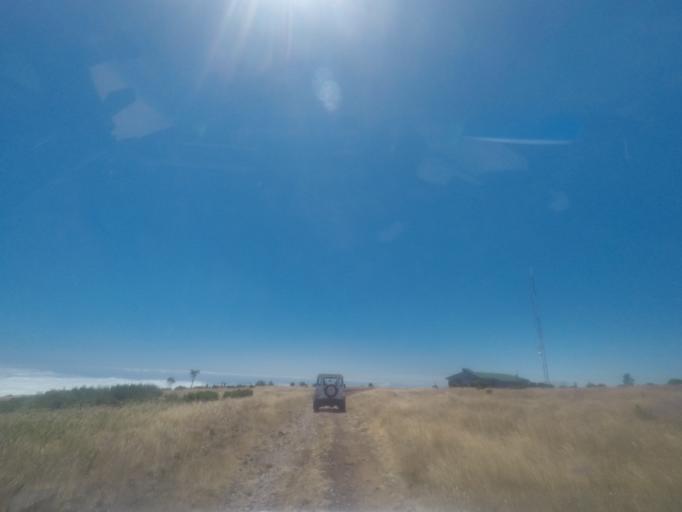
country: PT
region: Madeira
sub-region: Camara de Lobos
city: Curral das Freiras
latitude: 32.7211
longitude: -16.9162
